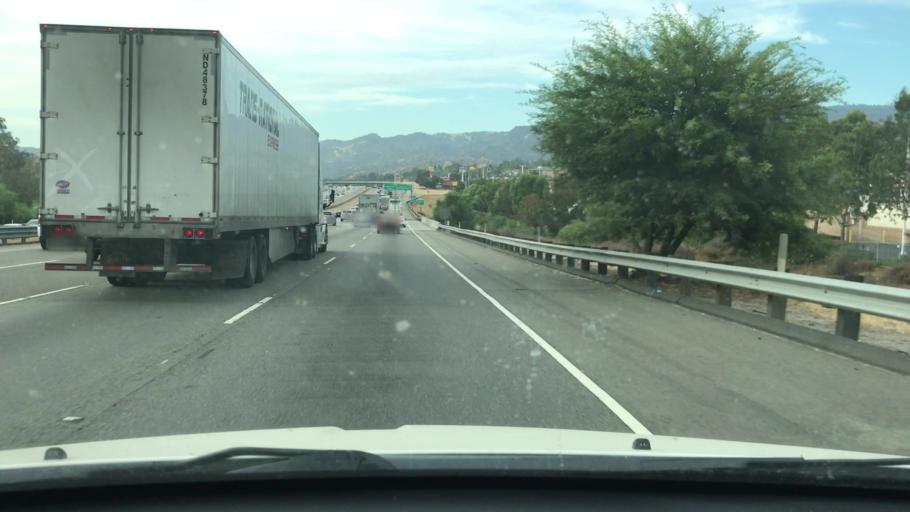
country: US
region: California
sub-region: Los Angeles County
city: Santa Clarita
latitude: 34.3872
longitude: -118.5696
